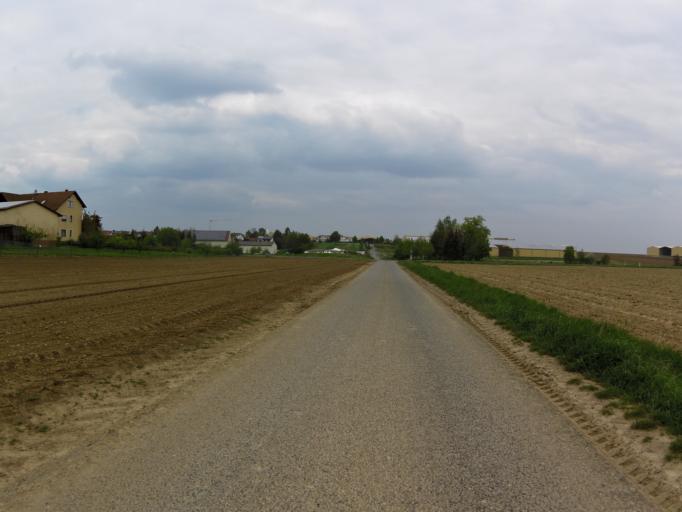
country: DE
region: Bavaria
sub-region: Regierungsbezirk Unterfranken
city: Unterpleichfeld
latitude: 49.8664
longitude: 10.0529
